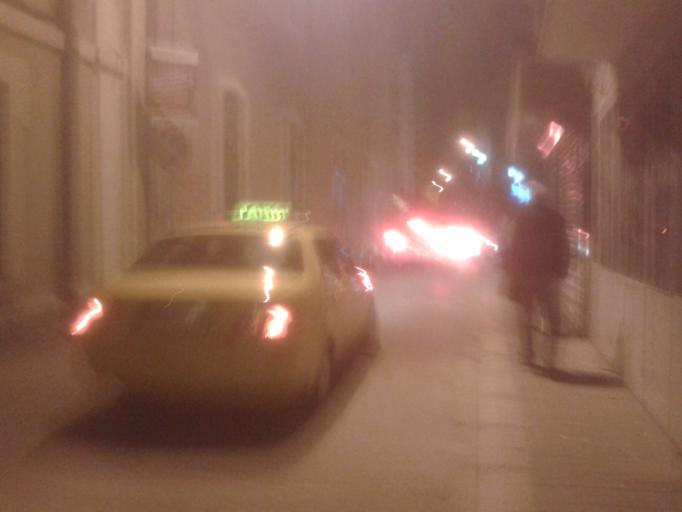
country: TR
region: Izmir
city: Izmir
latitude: 38.4399
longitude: 27.1451
